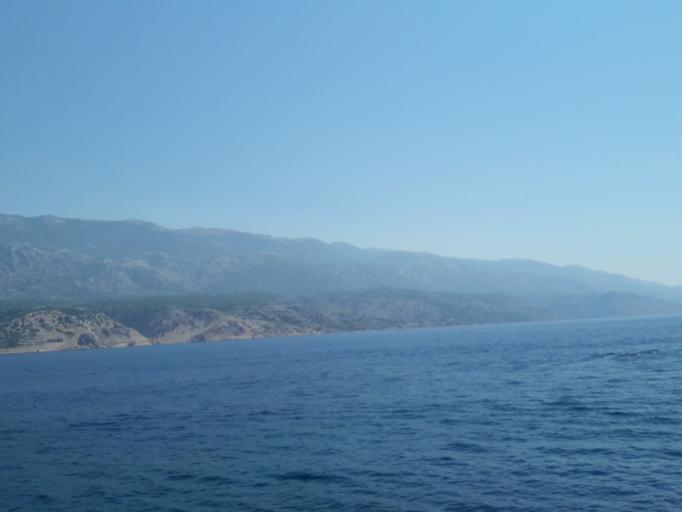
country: HR
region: Primorsko-Goranska
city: Banjol
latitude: 44.7032
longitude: 14.8697
